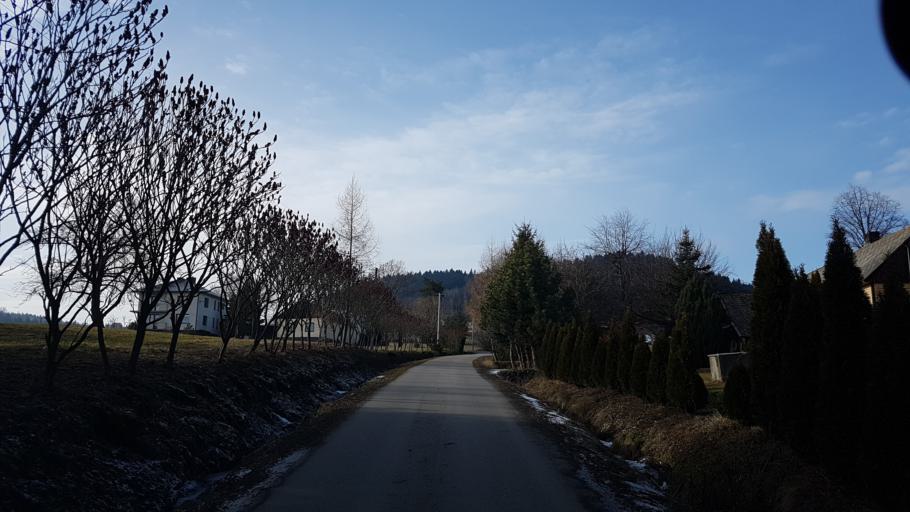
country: PL
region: Lesser Poland Voivodeship
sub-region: Powiat limanowski
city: Lukowica
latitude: 49.6589
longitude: 20.4726
